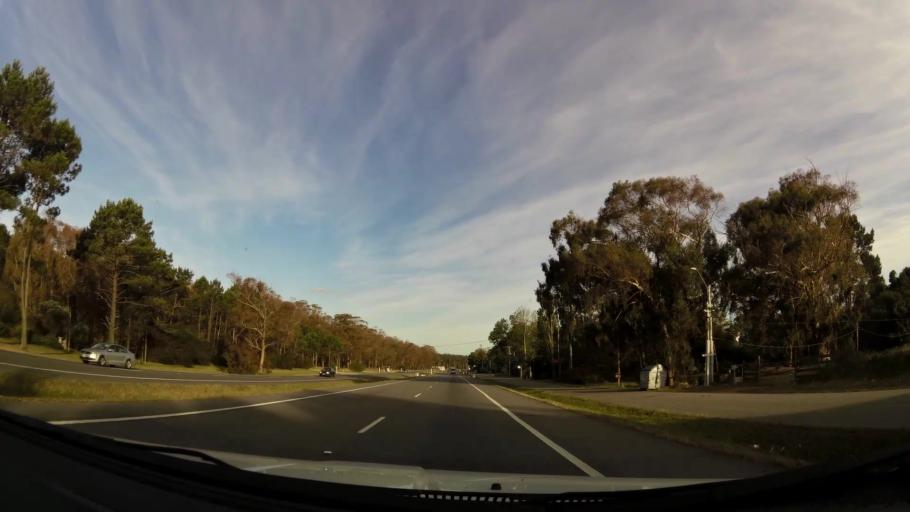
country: UY
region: Maldonado
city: Maldonado
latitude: -34.8767
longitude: -55.0598
